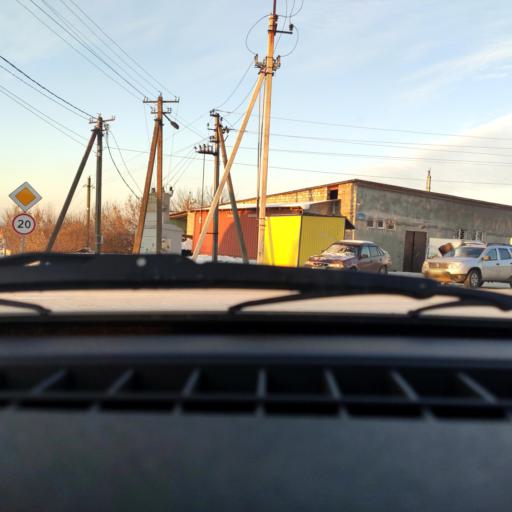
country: RU
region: Bashkortostan
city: Iglino
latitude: 54.7974
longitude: 56.3046
